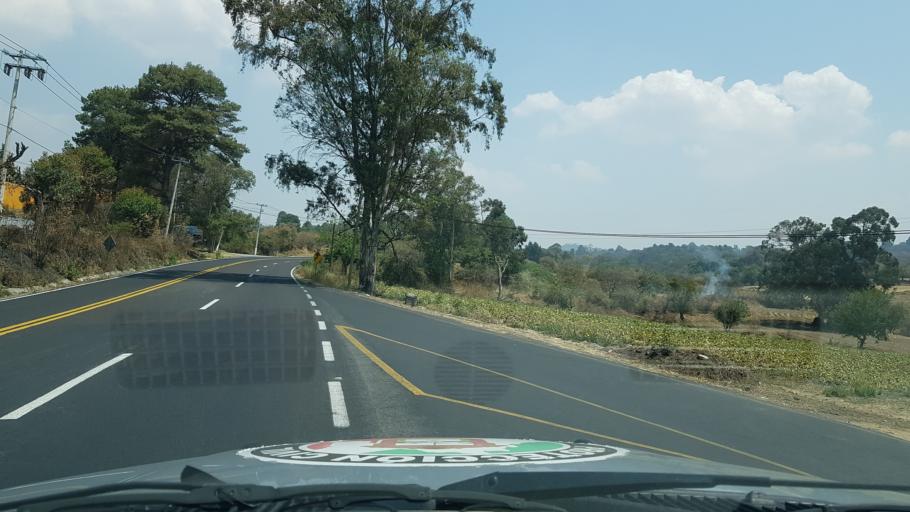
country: MX
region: Mexico
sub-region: Tepetlixpa
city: Nepantla de Sor Juana Ines de la Cruz
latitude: 18.9916
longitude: -98.8252
